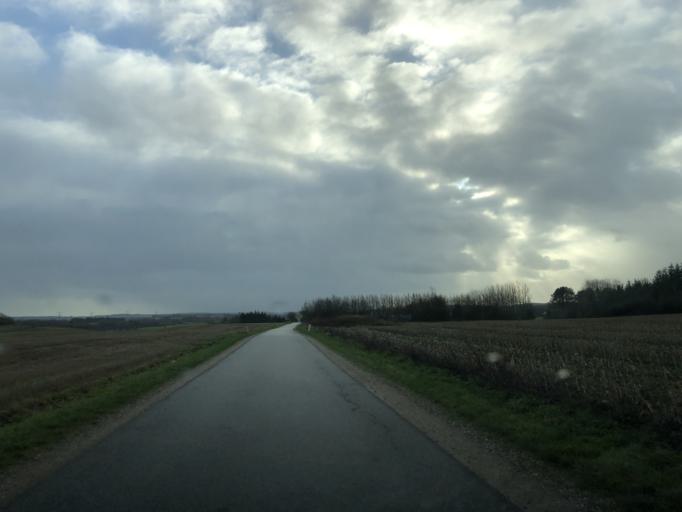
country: DK
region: North Denmark
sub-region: Rebild Kommune
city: Stovring
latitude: 56.9108
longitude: 9.7794
